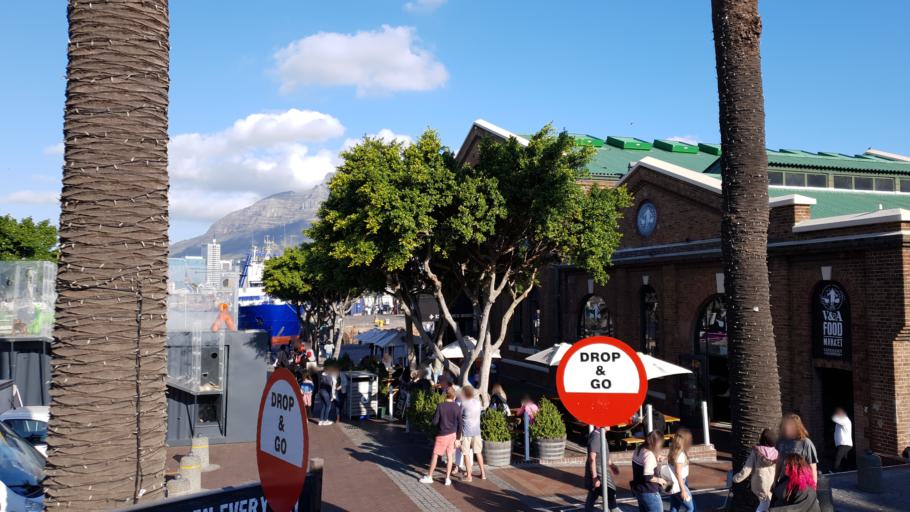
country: ZA
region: Western Cape
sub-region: City of Cape Town
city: Cape Town
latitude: -33.9058
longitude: 18.4196
